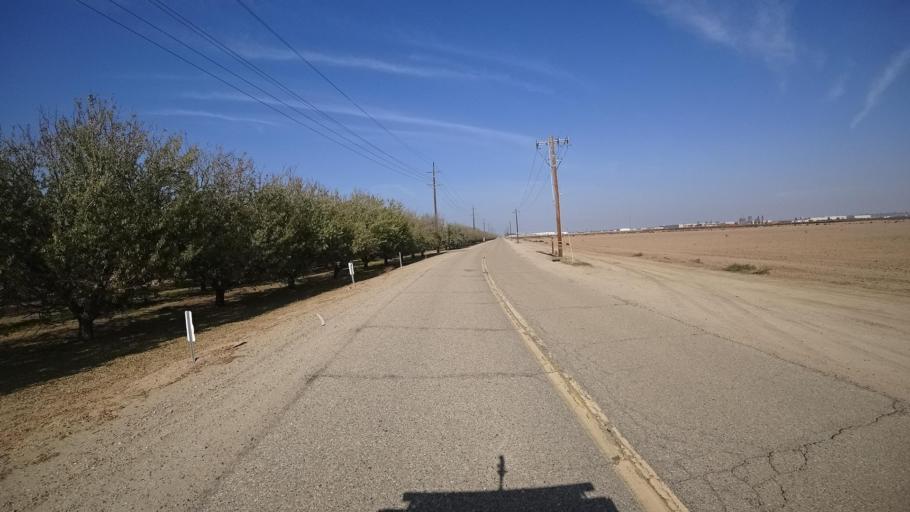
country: US
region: California
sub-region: Kern County
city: Rosedale
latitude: 35.4926
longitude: -119.1523
